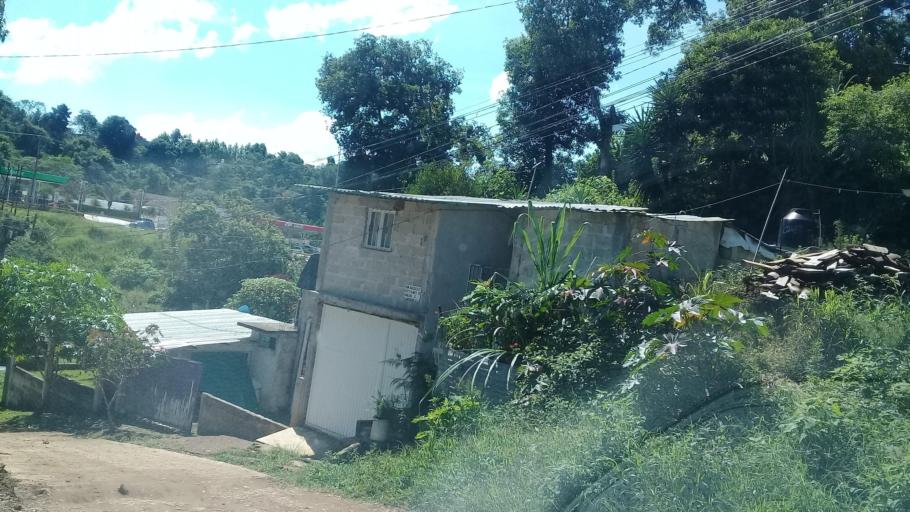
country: MX
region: Veracruz
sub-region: Xalapa
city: Xalapa de Enriquez
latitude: 19.5141
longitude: -96.9323
